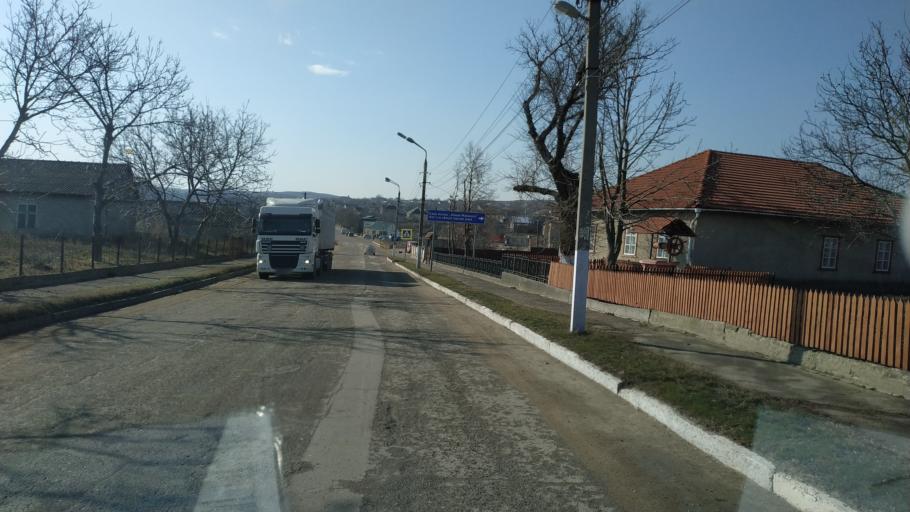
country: MD
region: Chisinau
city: Singera
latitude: 46.6827
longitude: 29.0476
